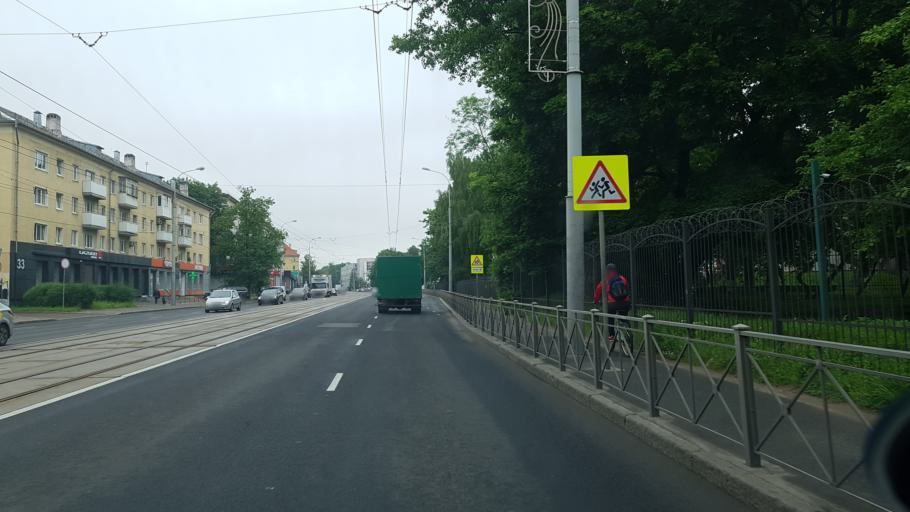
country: RU
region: Kaliningrad
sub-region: Gorod Kaliningrad
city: Kaliningrad
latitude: 54.7279
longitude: 20.4935
